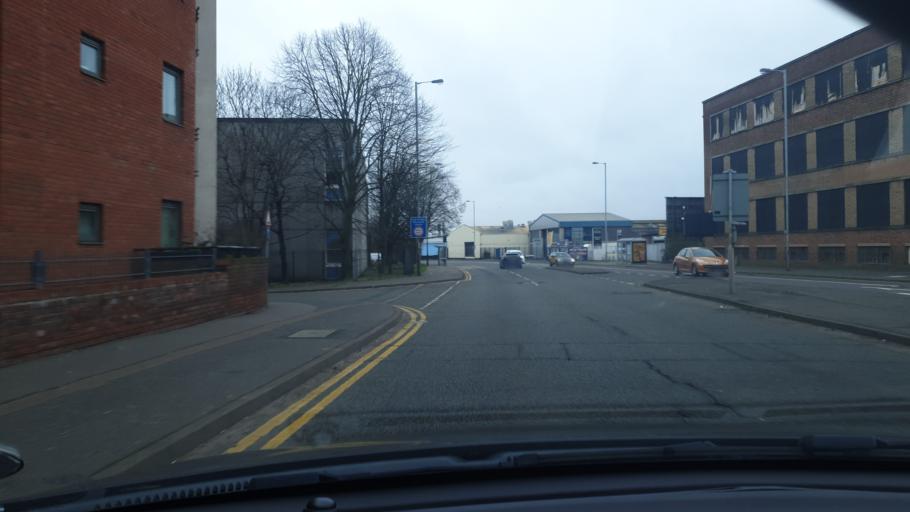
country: GB
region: England
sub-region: Wolverhampton
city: Wolverhampton
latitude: 52.5853
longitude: -2.1178
